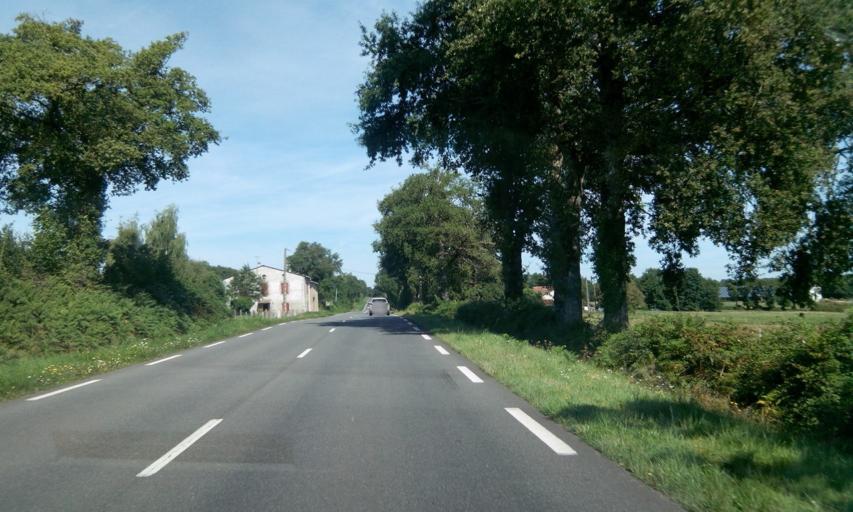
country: FR
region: Poitou-Charentes
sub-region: Departement de la Charente
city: Confolens
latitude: 46.0356
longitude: 0.6363
